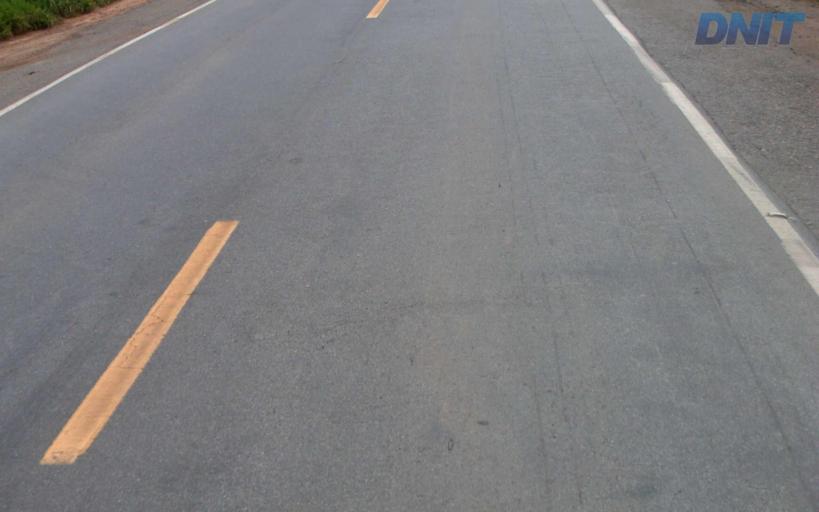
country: BR
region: Minas Gerais
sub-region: Governador Valadares
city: Governador Valadares
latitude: -18.9803
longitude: -42.1021
